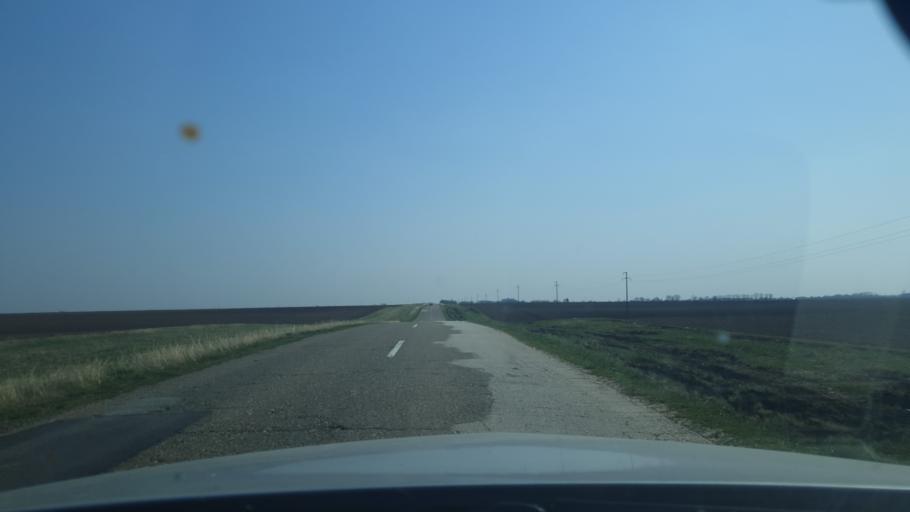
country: RS
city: Sasinci
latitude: 45.0314
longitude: 19.7496
